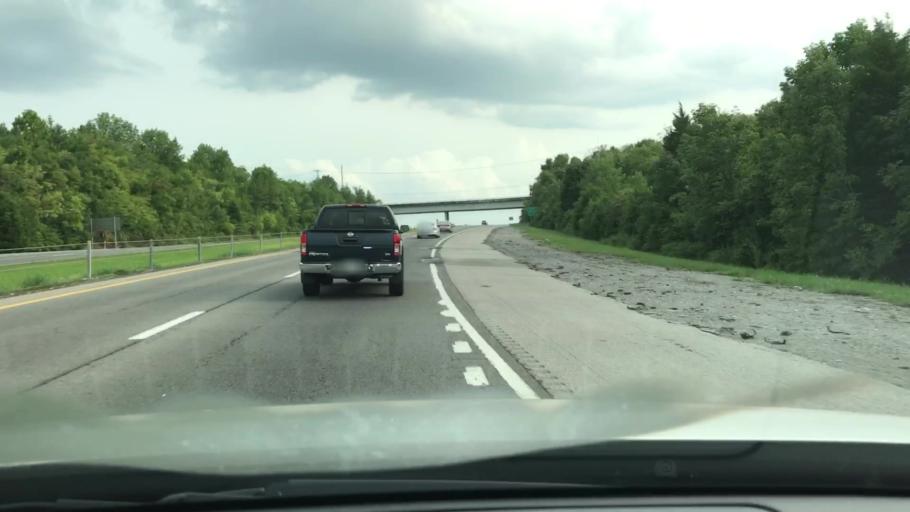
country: US
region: Tennessee
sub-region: Davidson County
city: Nashville
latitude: 36.2247
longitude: -86.7463
